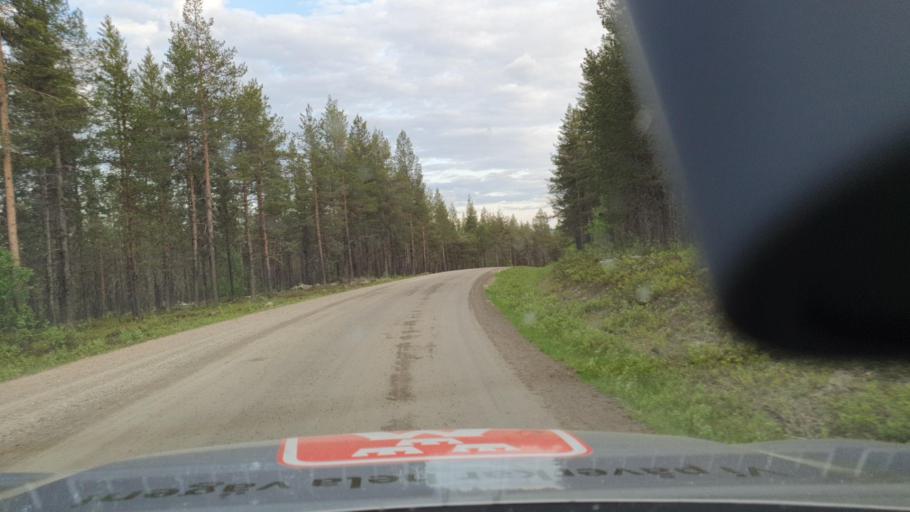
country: SE
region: Norrbotten
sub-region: Gallivare Kommun
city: Gaellivare
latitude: 66.7012
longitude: 21.1660
